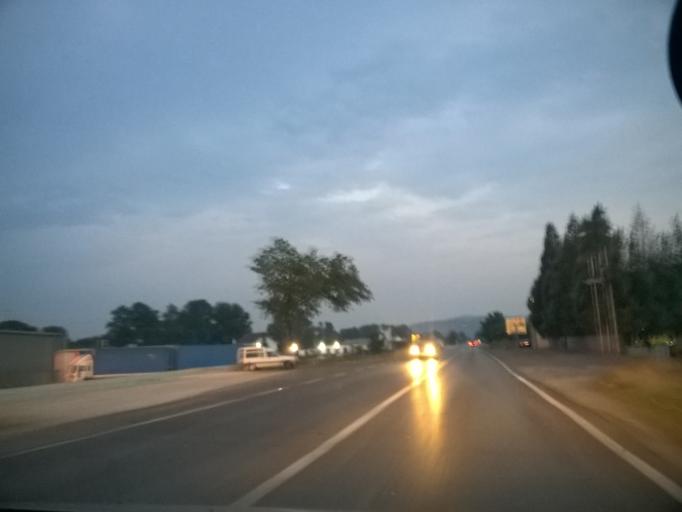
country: ME
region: Danilovgrad
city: Danilovgrad
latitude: 42.5307
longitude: 19.1160
